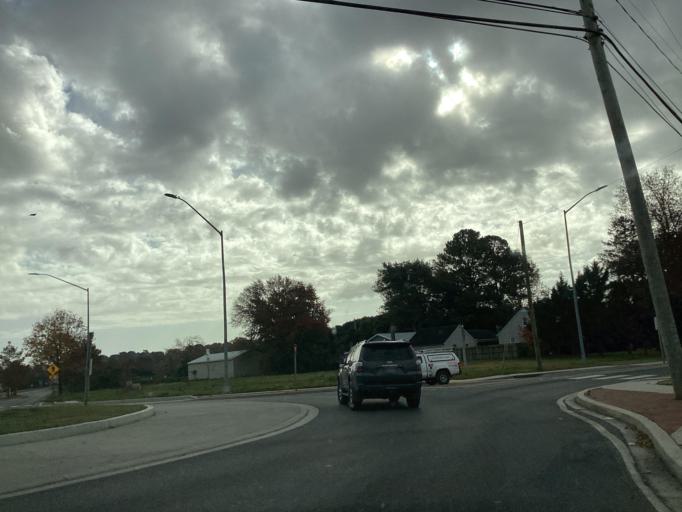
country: US
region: Maryland
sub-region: Somerset County
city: Princess Anne
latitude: 38.2193
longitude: -75.6962
